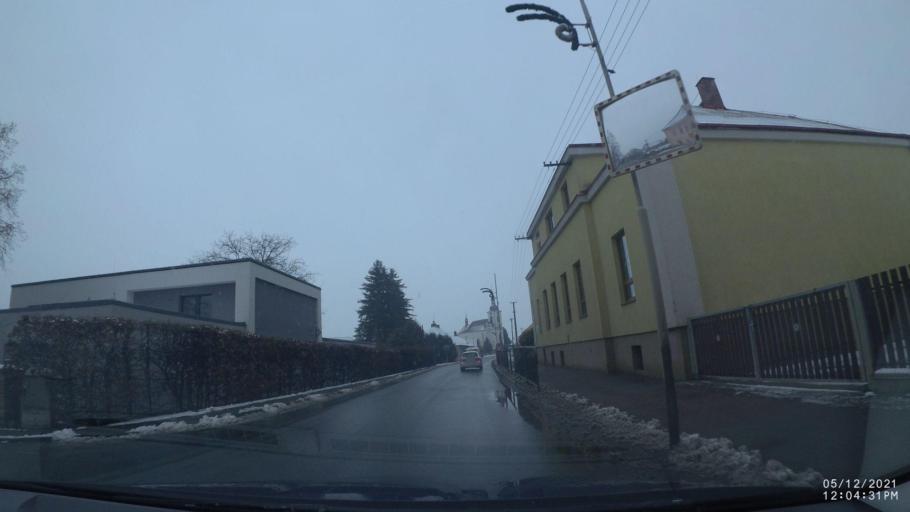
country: CZ
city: Ceske Mezirici
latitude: 50.2852
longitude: 16.0475
